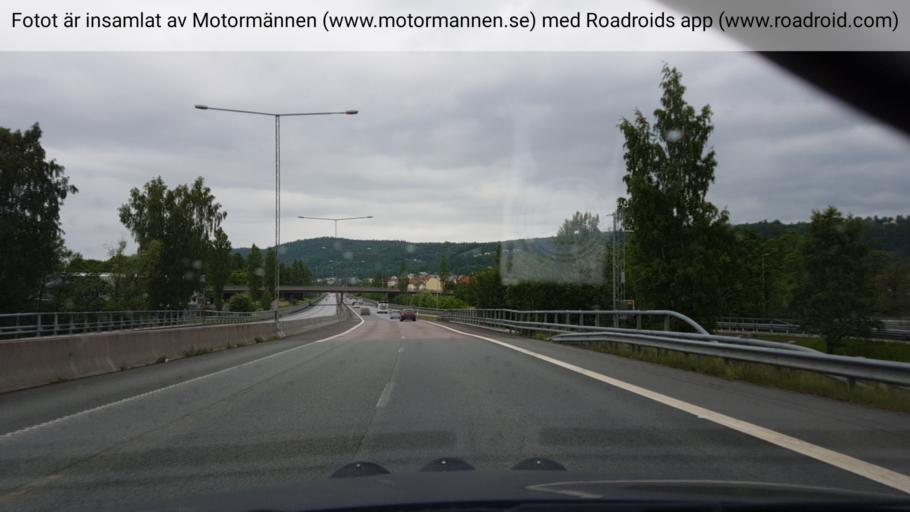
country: SE
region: Joenkoeping
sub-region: Jonkopings Kommun
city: Huskvarna
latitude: 57.7899
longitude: 14.2634
